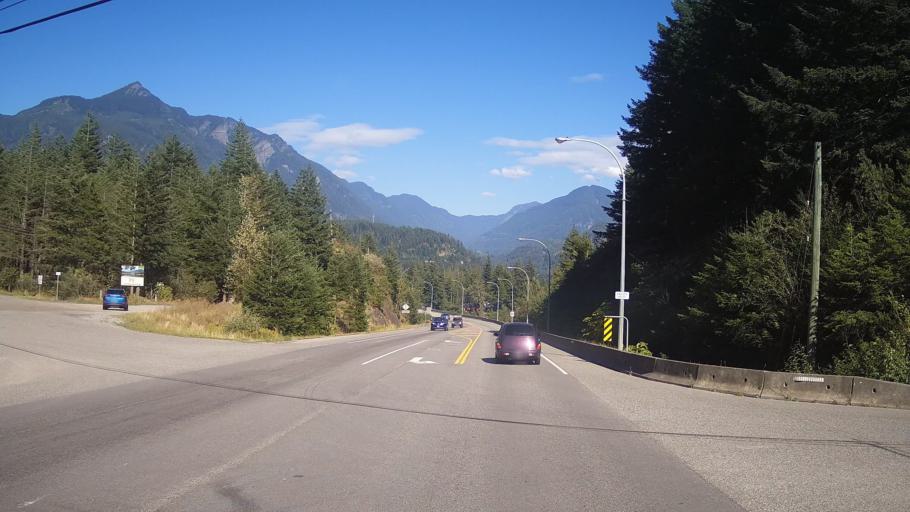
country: CA
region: British Columbia
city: Hope
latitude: 49.3861
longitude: -121.4575
